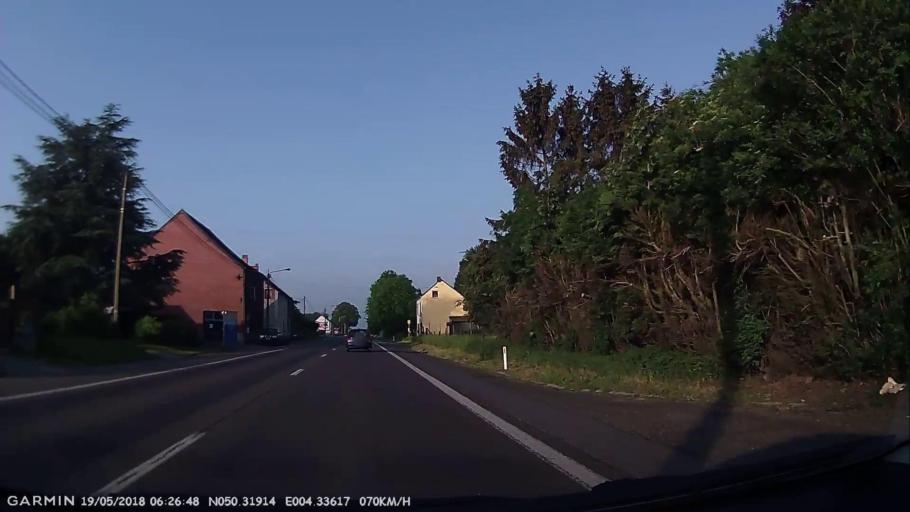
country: BE
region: Wallonia
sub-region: Province du Hainaut
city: Thuin
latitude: 50.3190
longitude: 4.3361
